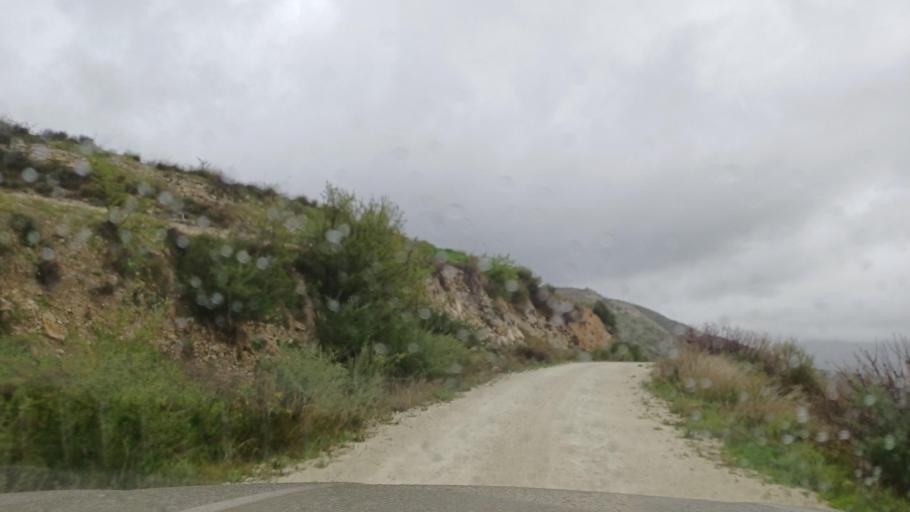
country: CY
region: Limassol
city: Pachna
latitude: 34.7950
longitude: 32.6942
